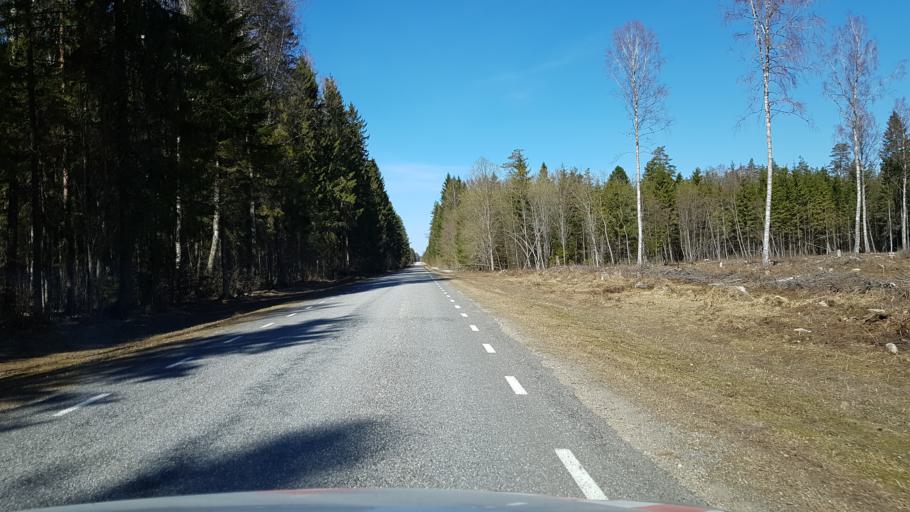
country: EE
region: Laeaene-Virumaa
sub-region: Vinni vald
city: Vinni
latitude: 59.1509
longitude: 26.5185
